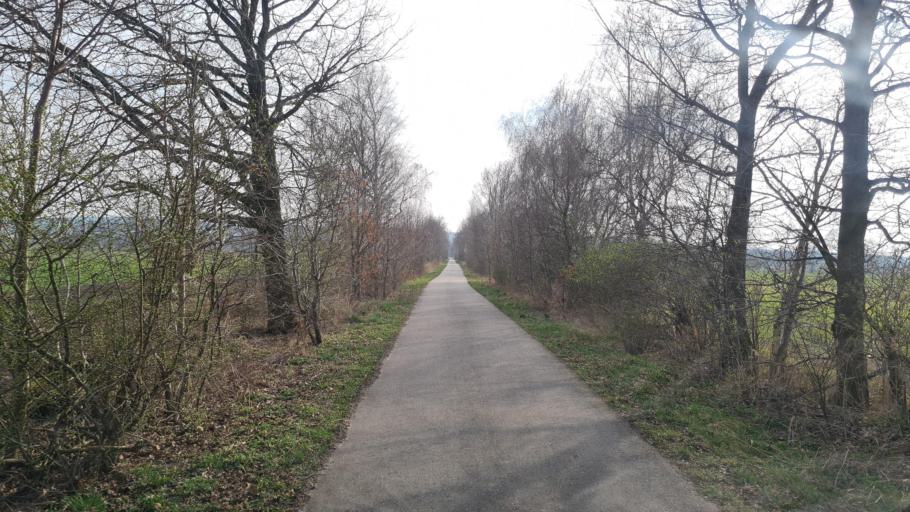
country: DE
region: Brandenburg
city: Groden
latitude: 51.4176
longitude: 13.5796
